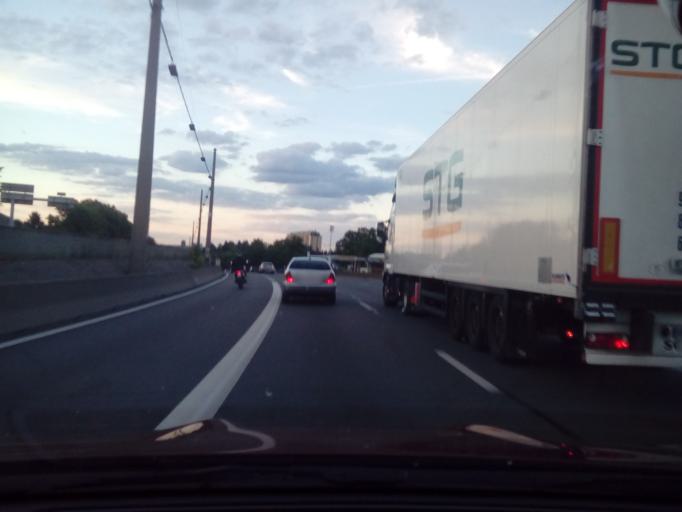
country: FR
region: Rhone-Alpes
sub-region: Departement du Rhone
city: Bron
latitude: 45.7380
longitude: 4.9041
